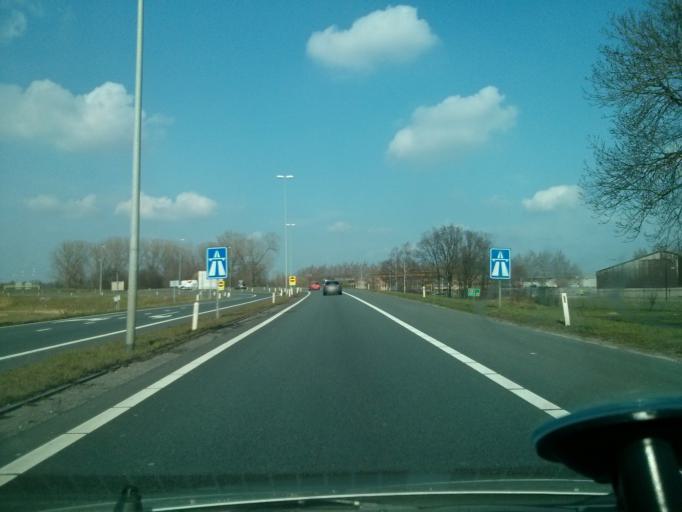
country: NL
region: North Brabant
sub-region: Gemeente Sint-Michielsgestel
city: Sint-Michielsgestel
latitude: 51.6846
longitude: 5.3509
